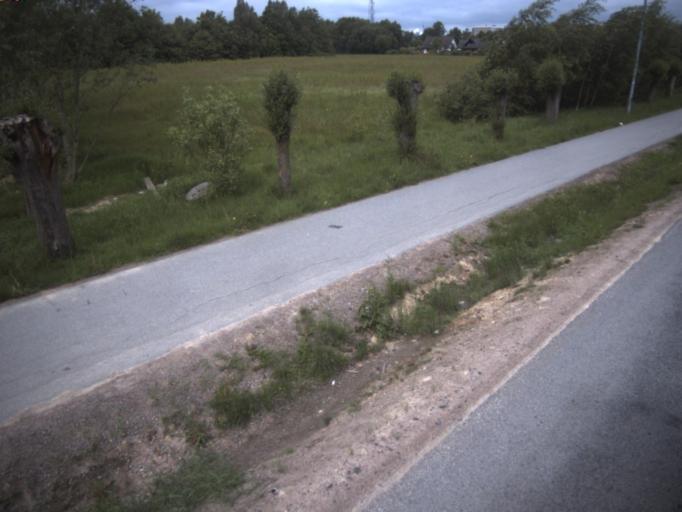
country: SE
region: Skane
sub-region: Helsingborg
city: Helsingborg
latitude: 56.0567
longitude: 12.7353
